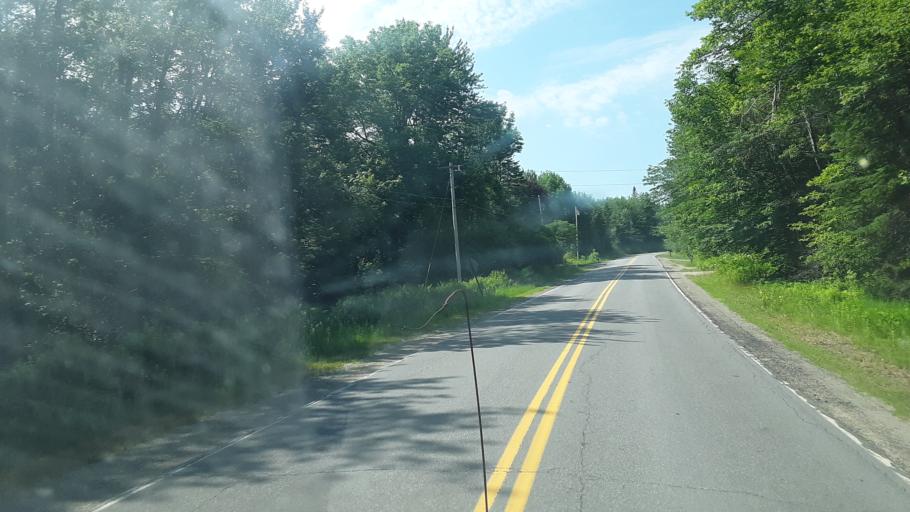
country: US
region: Maine
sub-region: Waldo County
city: Swanville
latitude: 44.5573
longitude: -68.9533
